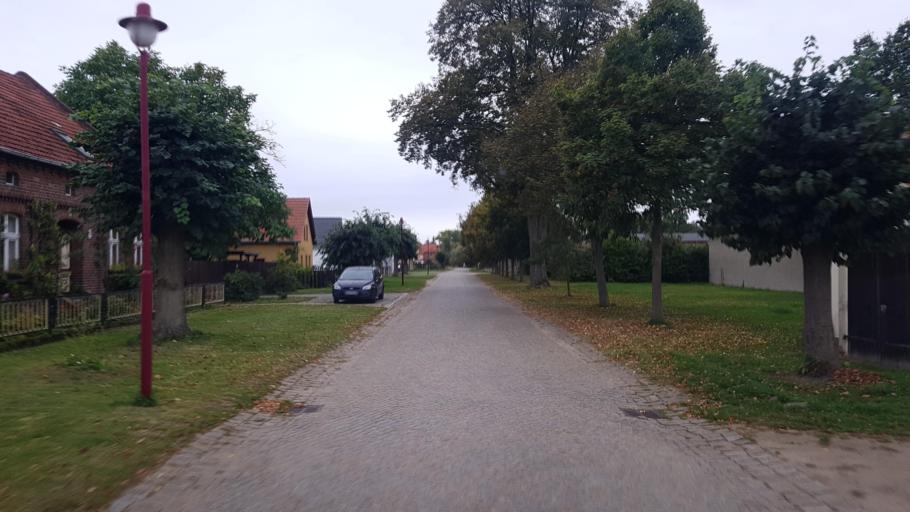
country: DE
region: Brandenburg
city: Drahnsdorf
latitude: 51.8925
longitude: 13.6435
